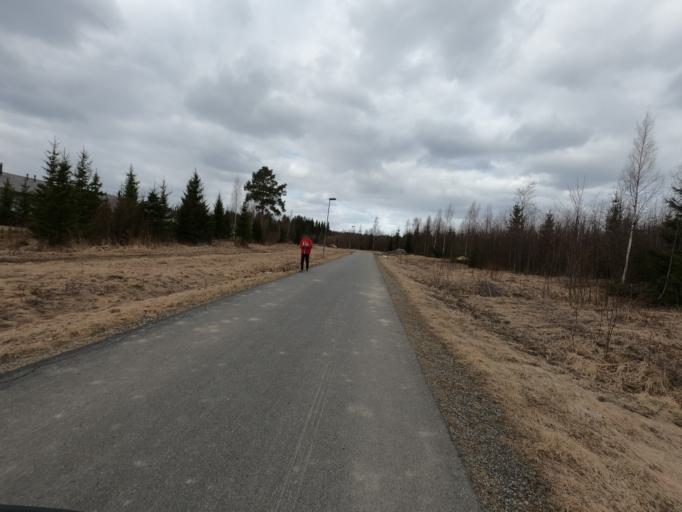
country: FI
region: North Karelia
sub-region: Joensuu
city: Joensuu
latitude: 62.5671
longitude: 29.8173
